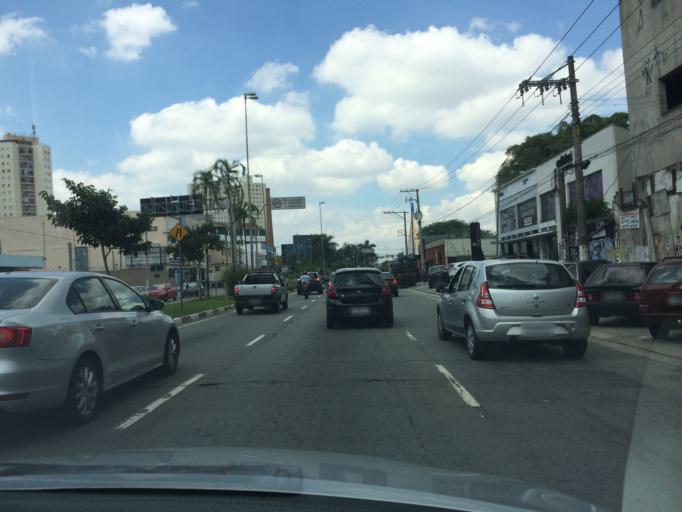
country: BR
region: Sao Paulo
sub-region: Guarulhos
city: Guarulhos
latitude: -23.4684
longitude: -46.5218
